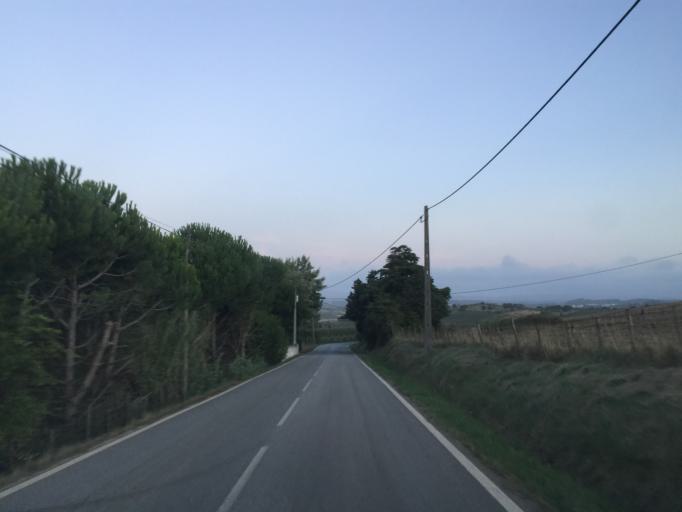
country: PT
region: Leiria
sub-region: Bombarral
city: Bombarral
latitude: 39.2772
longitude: -9.1861
